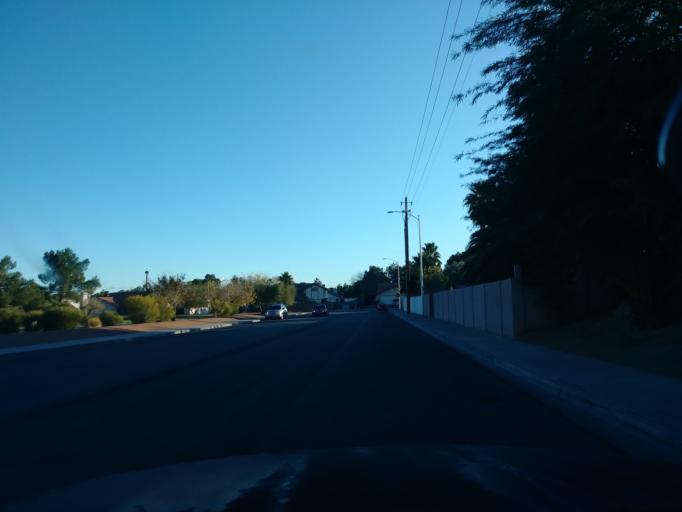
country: US
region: Nevada
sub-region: Clark County
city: Spring Valley
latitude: 36.1490
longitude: -115.2387
